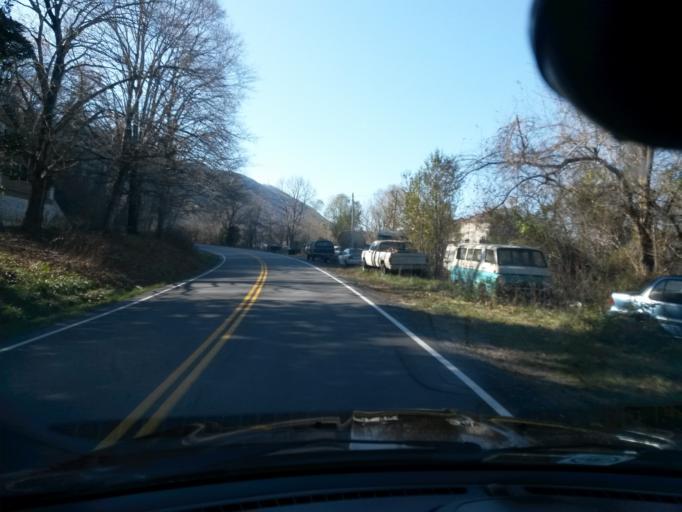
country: US
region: Virginia
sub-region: Alleghany County
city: Clifton Forge
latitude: 37.6526
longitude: -79.8073
